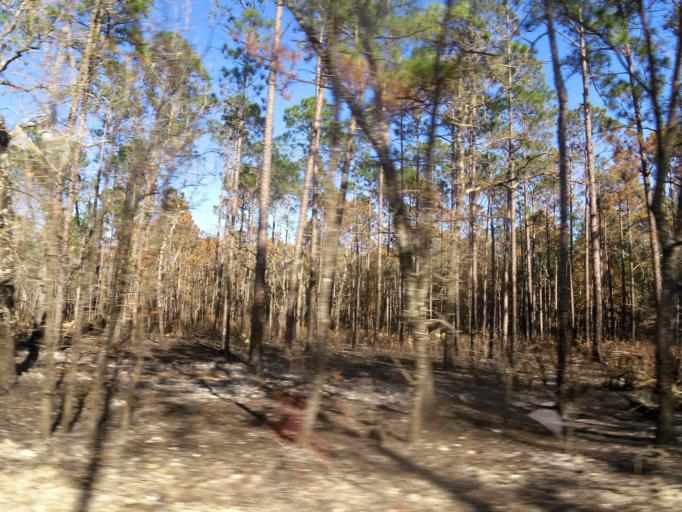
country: US
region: Florida
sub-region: Clay County
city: Middleburg
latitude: 30.1501
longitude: -81.8821
